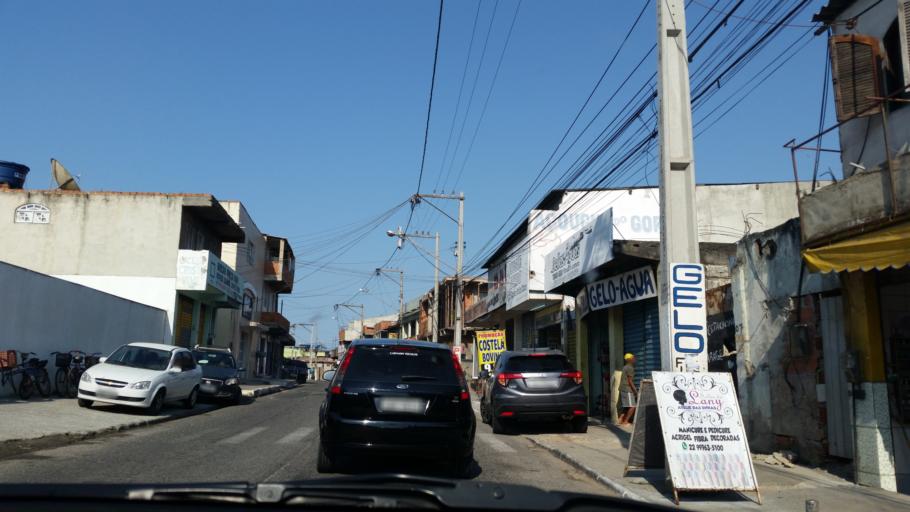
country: BR
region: Rio de Janeiro
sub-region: Cabo Frio
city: Cabo Frio
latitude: -22.8666
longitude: -42.0179
